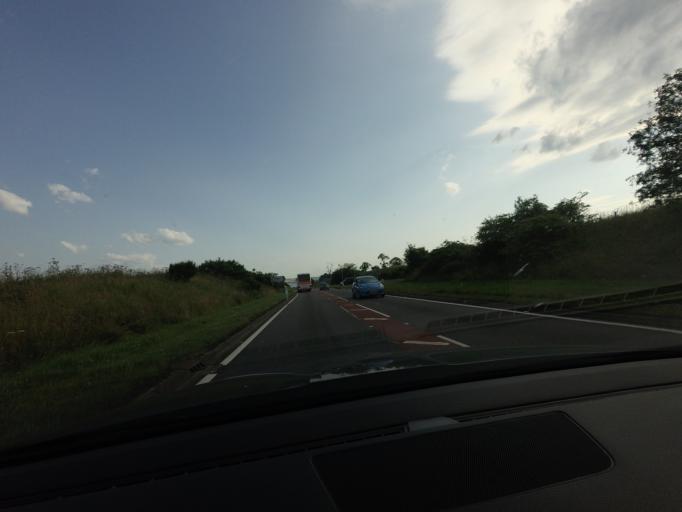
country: GB
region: Scotland
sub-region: Highland
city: Evanton
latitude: 57.6522
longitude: -4.3393
